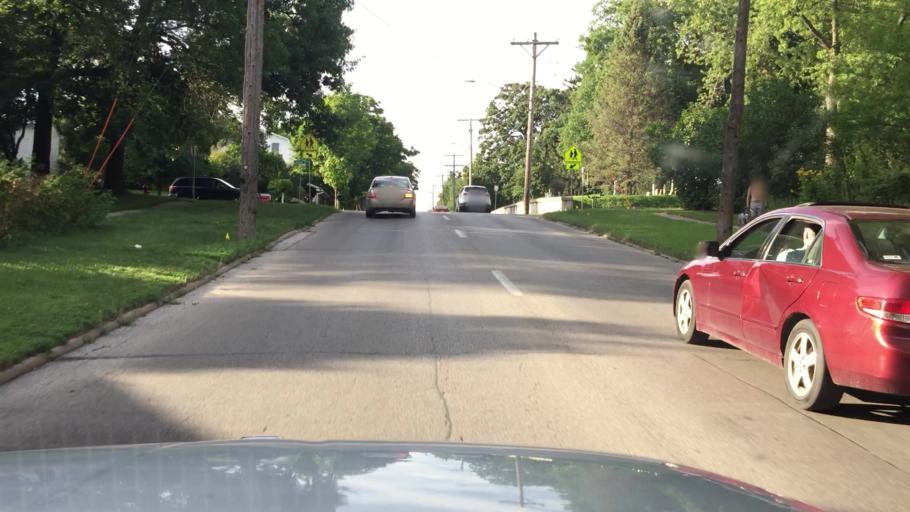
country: US
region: Iowa
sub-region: Johnson County
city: Iowa City
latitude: 41.6675
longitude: -91.5228
